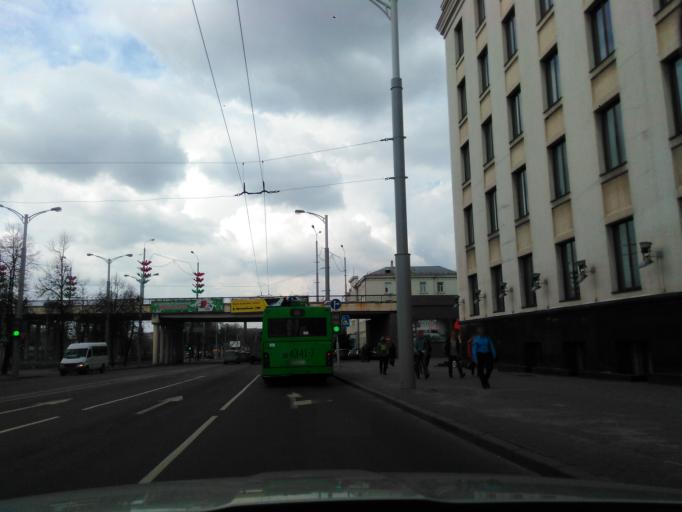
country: BY
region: Minsk
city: Minsk
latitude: 53.8926
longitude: 27.5451
